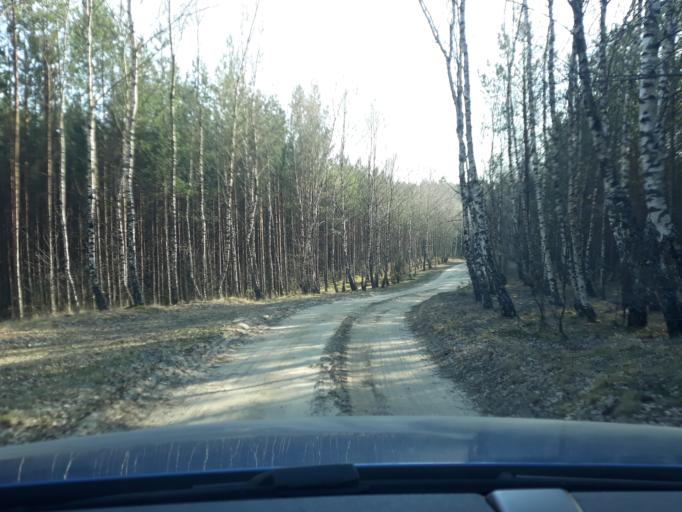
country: PL
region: Pomeranian Voivodeship
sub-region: Powiat bytowski
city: Lipnica
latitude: 53.8878
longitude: 17.4901
